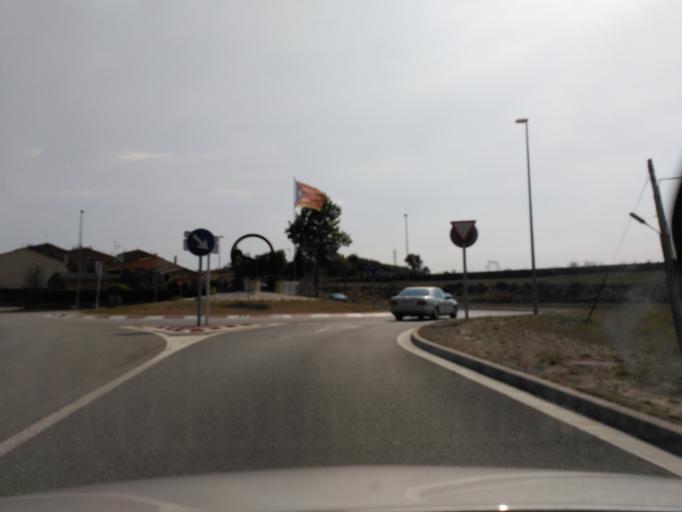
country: ES
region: Catalonia
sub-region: Provincia de Barcelona
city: Manlleu
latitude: 41.9743
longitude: 2.3017
